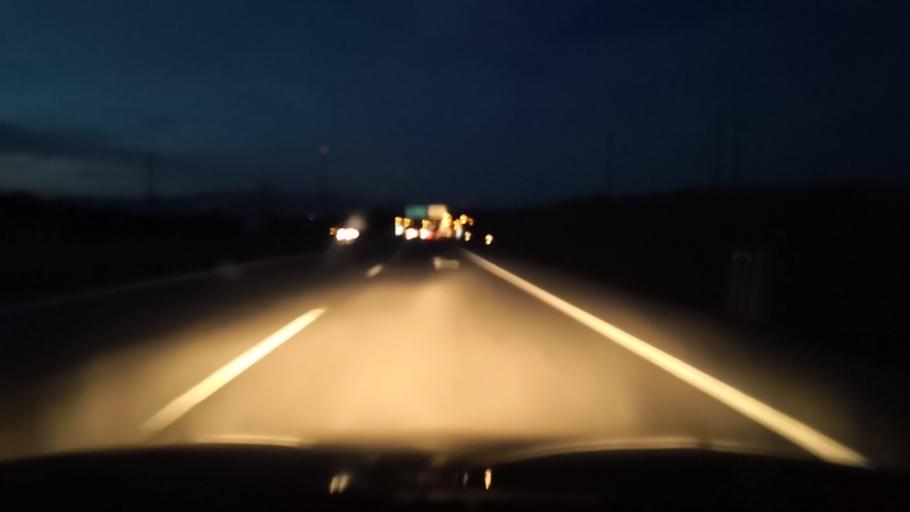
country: PT
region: Guarda
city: Alcains
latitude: 39.9132
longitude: -7.4770
